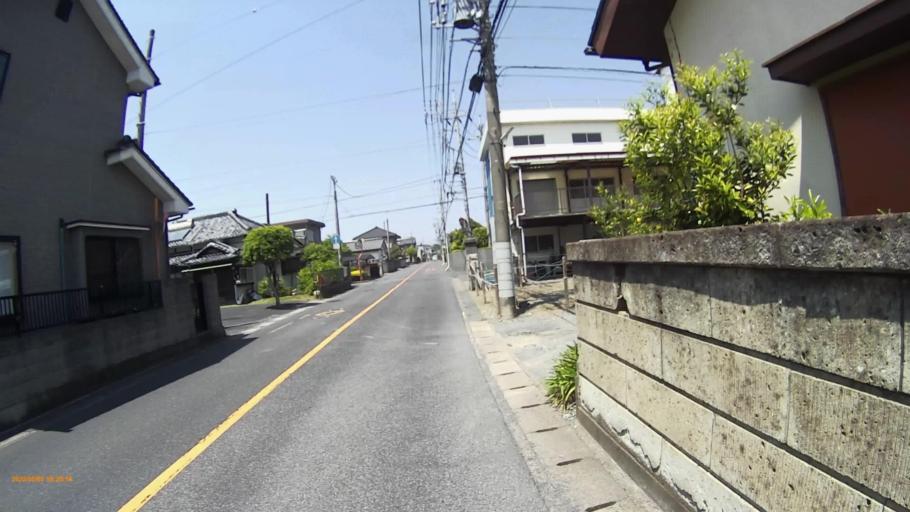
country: JP
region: Saitama
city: Koshigaya
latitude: 35.9249
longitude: 139.7812
